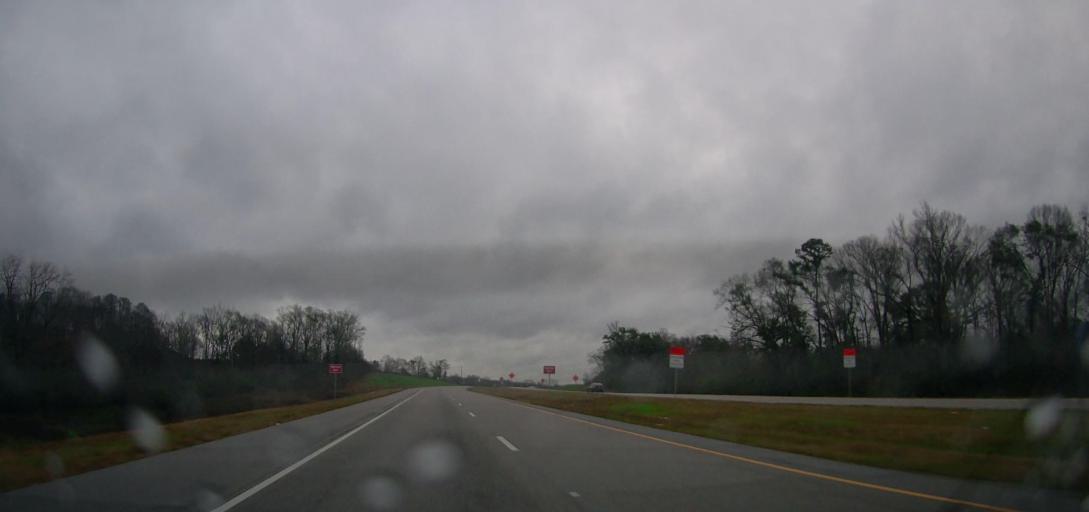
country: US
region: Alabama
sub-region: Bibb County
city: Centreville
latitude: 32.9400
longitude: -87.0706
